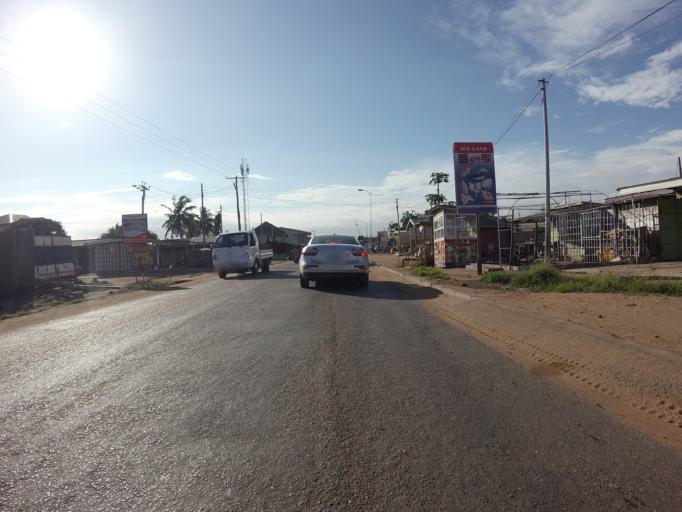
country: GH
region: Greater Accra
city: Nungua
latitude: 5.6480
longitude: -0.0622
